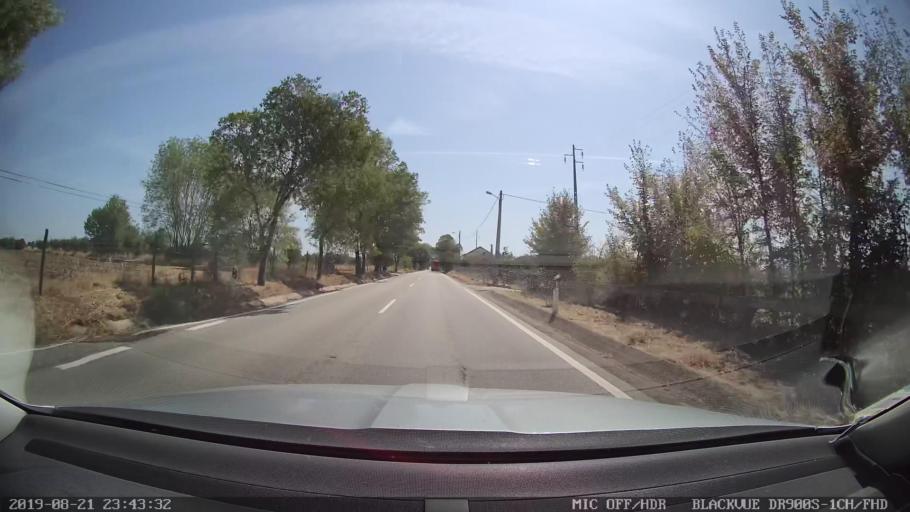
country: PT
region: Castelo Branco
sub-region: Idanha-A-Nova
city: Idanha-a-Nova
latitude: 39.8495
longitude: -7.2926
